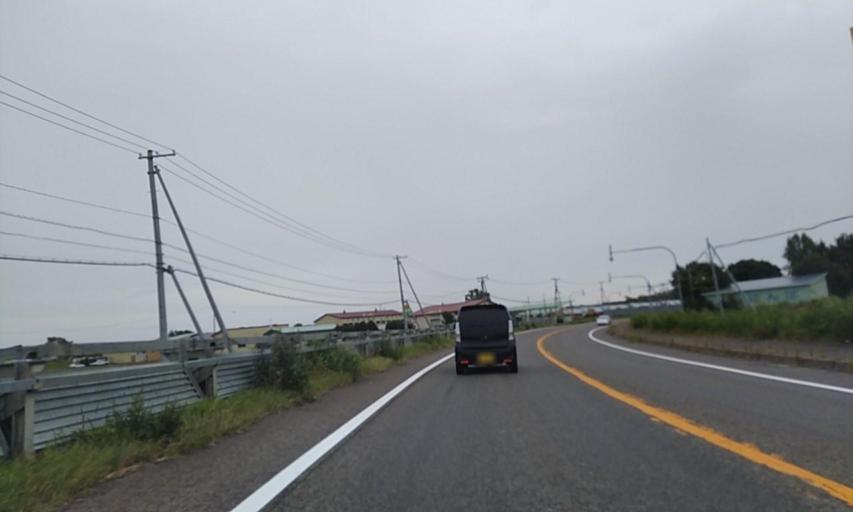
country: JP
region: Hokkaido
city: Bihoro
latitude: 43.9158
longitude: 144.1587
